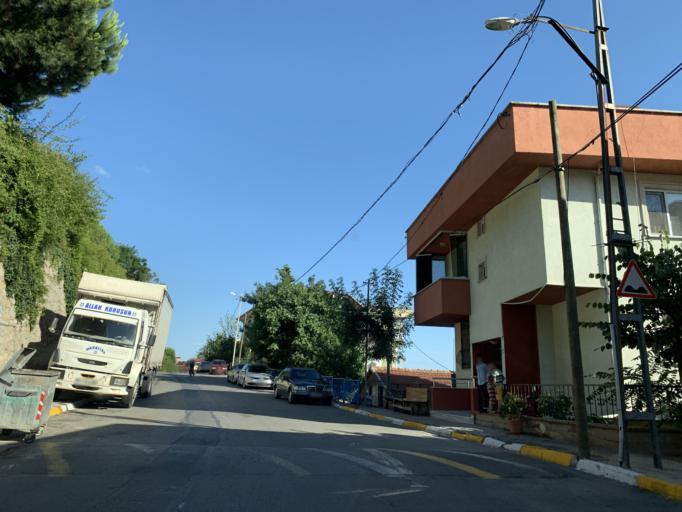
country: TR
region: Istanbul
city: Pendik
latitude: 40.8902
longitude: 29.2506
